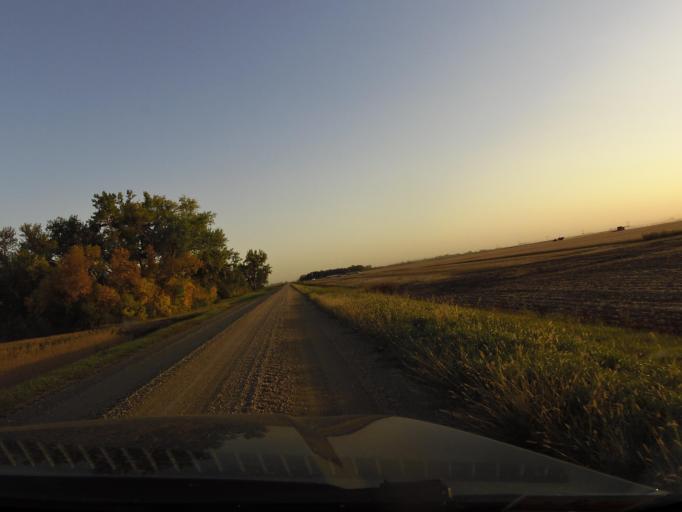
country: US
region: North Dakota
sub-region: Walsh County
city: Grafton
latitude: 48.3909
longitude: -97.2555
